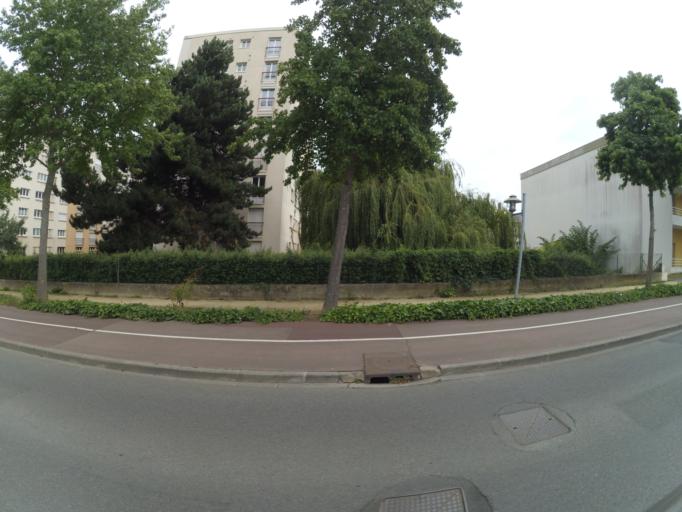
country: FR
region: Brittany
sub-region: Departement des Cotes-d'Armor
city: Saint-Brieuc
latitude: 48.5091
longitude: -2.7742
